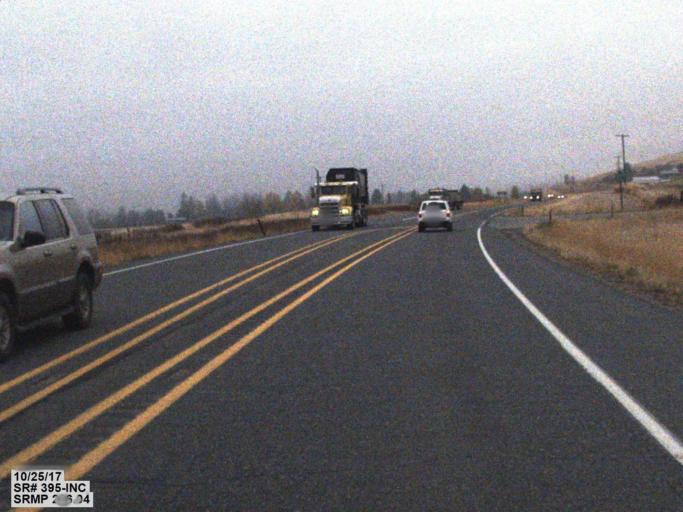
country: US
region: Washington
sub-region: Stevens County
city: Kettle Falls
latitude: 48.5996
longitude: -118.0147
